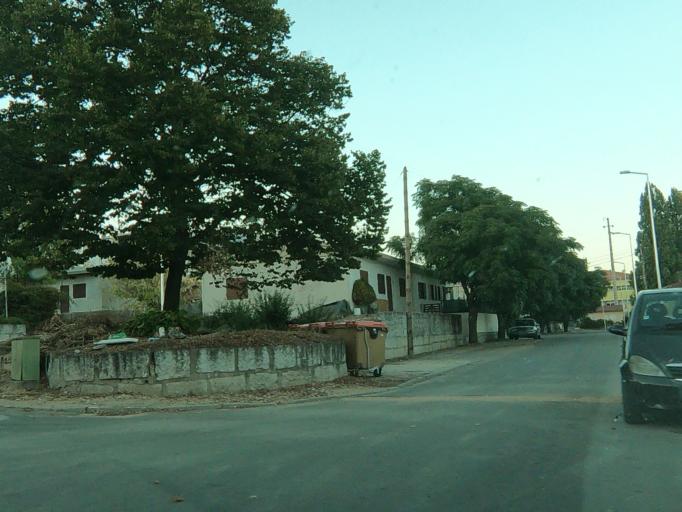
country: PT
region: Vila Real
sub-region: Vila Real
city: Vila Real
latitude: 41.3081
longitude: -7.7677
